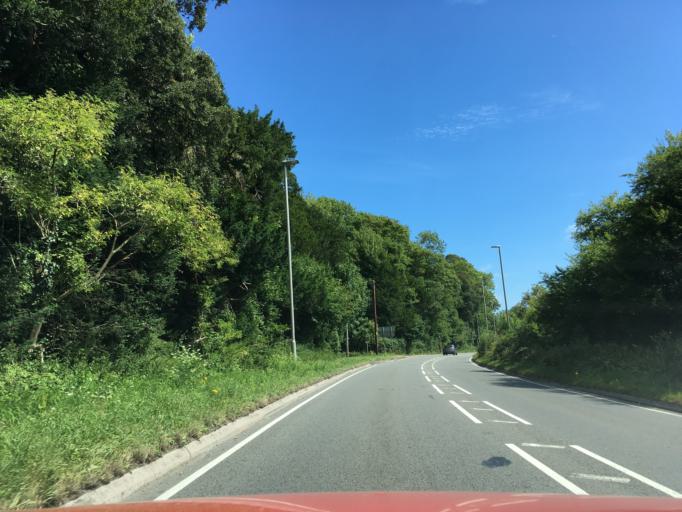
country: GB
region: England
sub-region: Dorset
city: Dorchester
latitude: 50.7495
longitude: -2.5127
